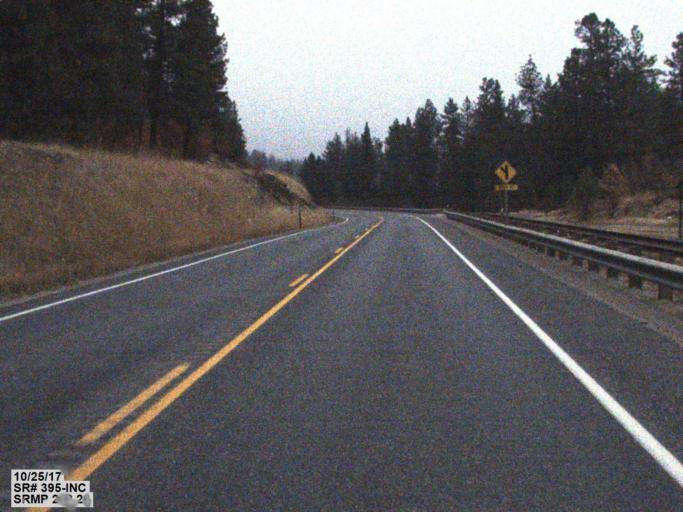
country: US
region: Washington
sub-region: Stevens County
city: Kettle Falls
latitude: 48.6325
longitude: -118.1207
